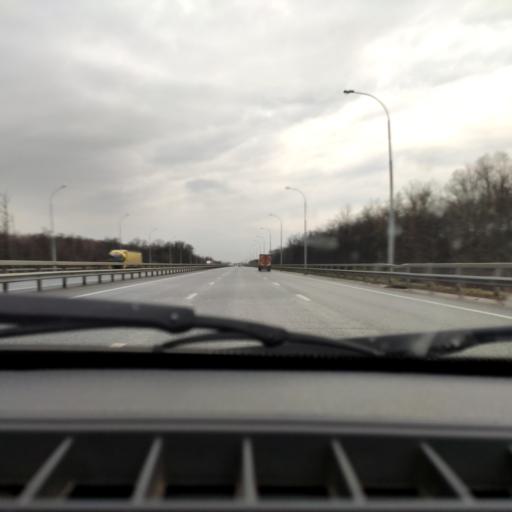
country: RU
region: Bashkortostan
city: Ufa
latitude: 54.6481
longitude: 56.0370
